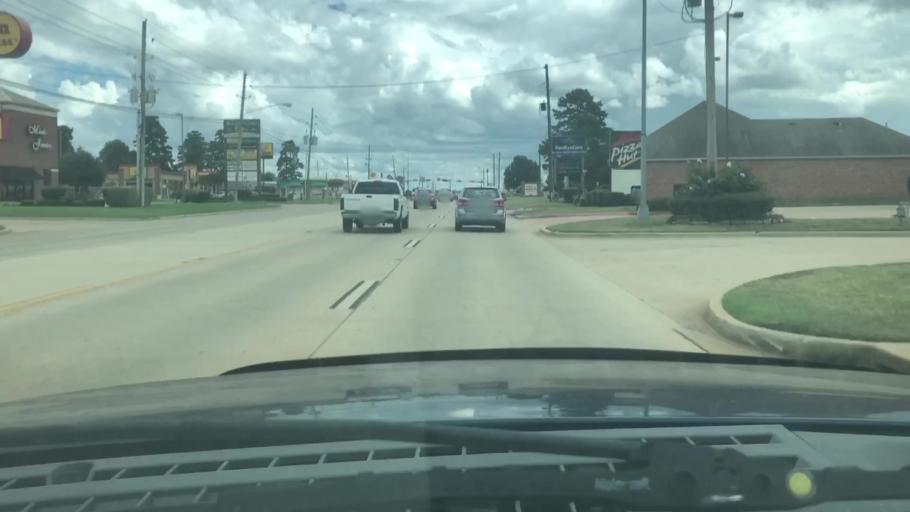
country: US
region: Texas
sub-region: Bowie County
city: Wake Village
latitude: 33.4622
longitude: -94.0926
